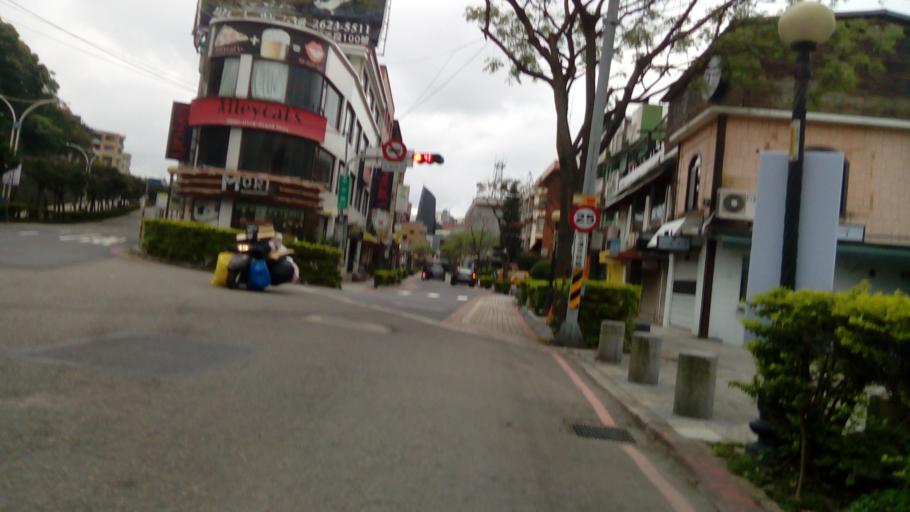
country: TW
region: Taipei
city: Taipei
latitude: 25.1734
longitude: 121.4353
